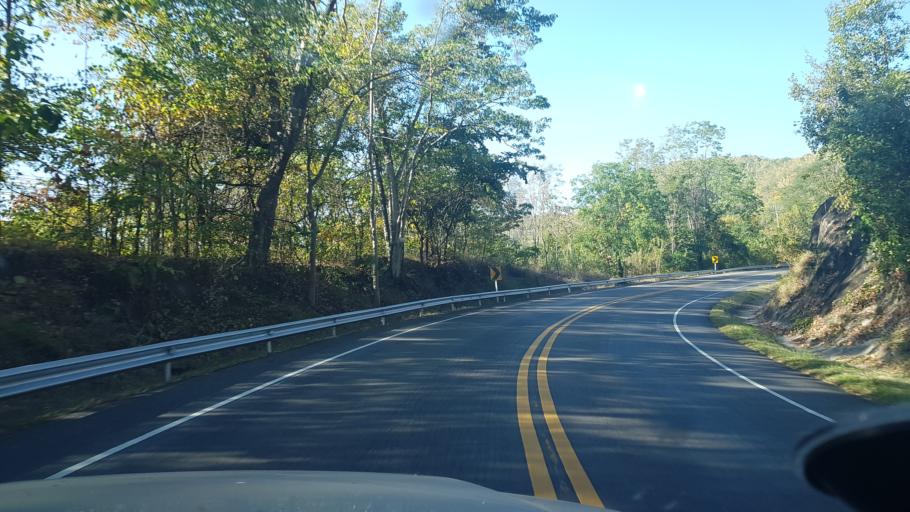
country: TH
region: Phetchabun
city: Lom Sak
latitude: 16.7430
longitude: 101.3933
